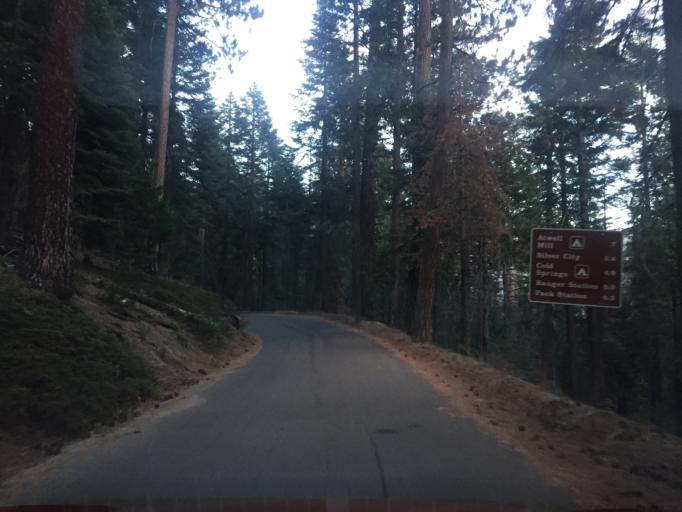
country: US
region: California
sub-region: Tulare County
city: Three Rivers
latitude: 36.4625
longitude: -118.6773
